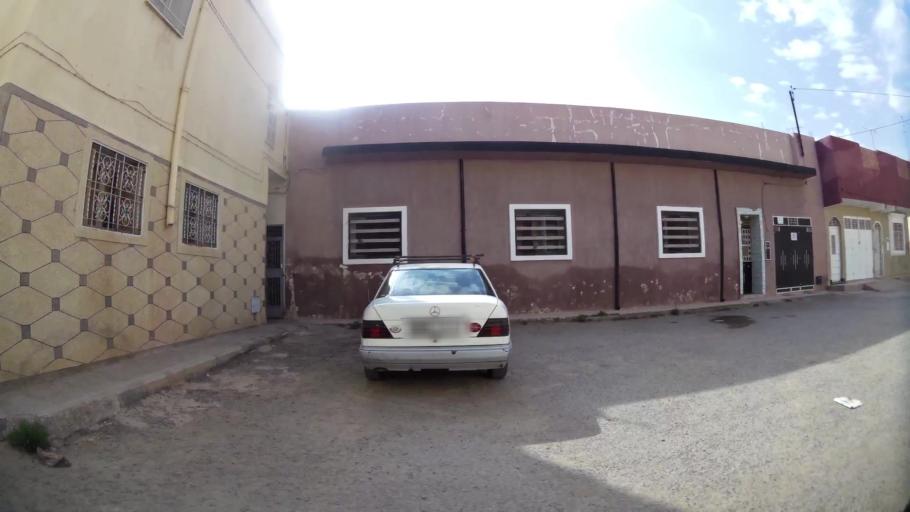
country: MA
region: Oriental
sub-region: Oujda-Angad
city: Oujda
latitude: 34.6905
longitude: -1.9047
